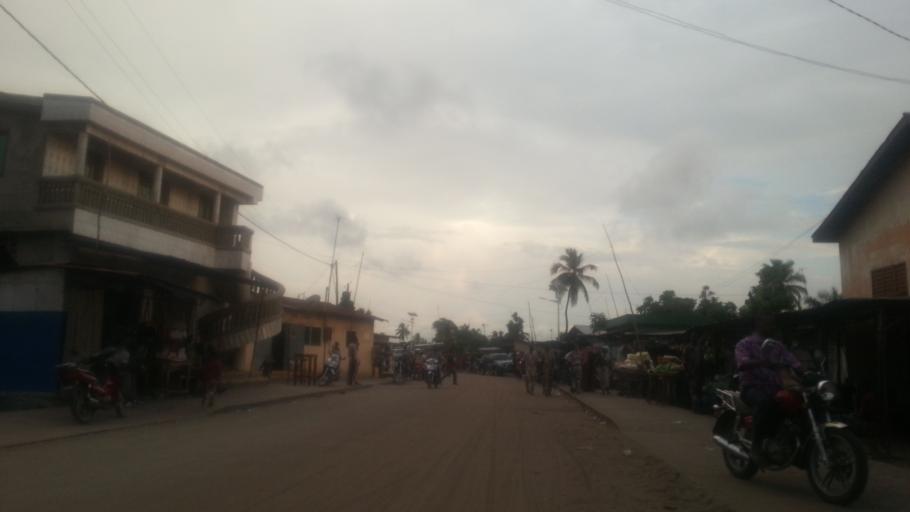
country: BJ
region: Queme
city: Porto-Novo
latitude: 6.3900
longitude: 2.5419
